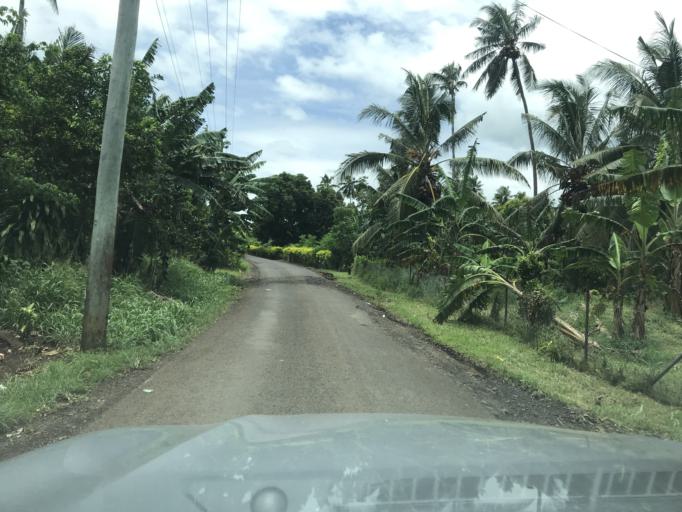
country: WS
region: Tuamasaga
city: Afenga
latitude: -13.8050
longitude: -171.8870
